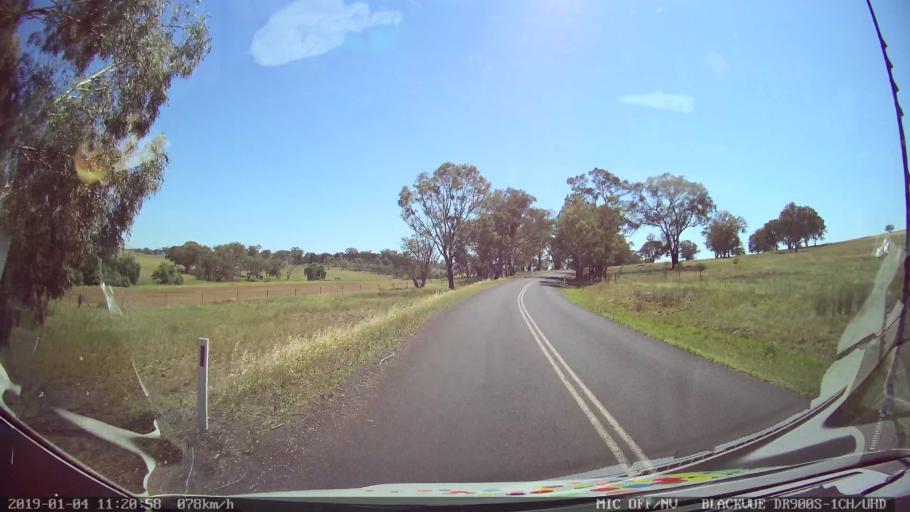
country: AU
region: New South Wales
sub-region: Cabonne
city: Molong
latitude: -33.1583
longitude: 148.7061
